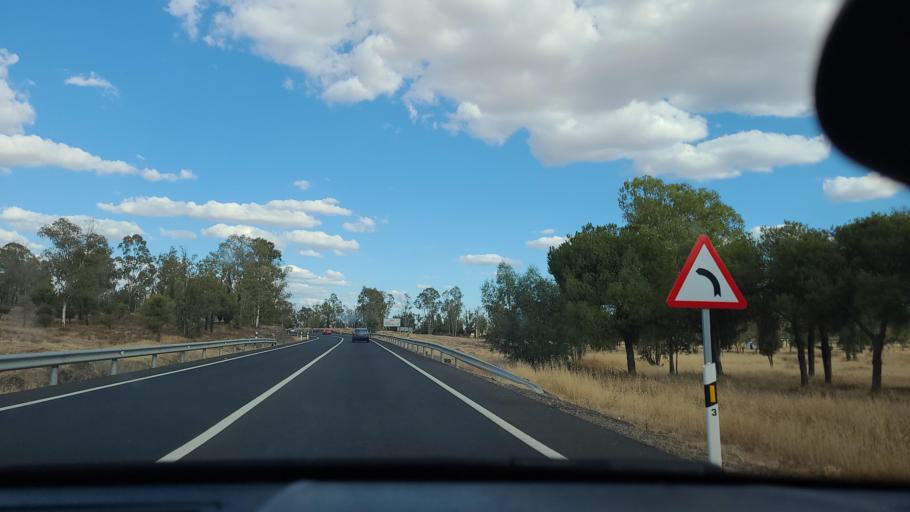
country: ES
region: Extremadura
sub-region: Provincia de Badajoz
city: Berlanga
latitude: 38.2729
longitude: -5.8140
